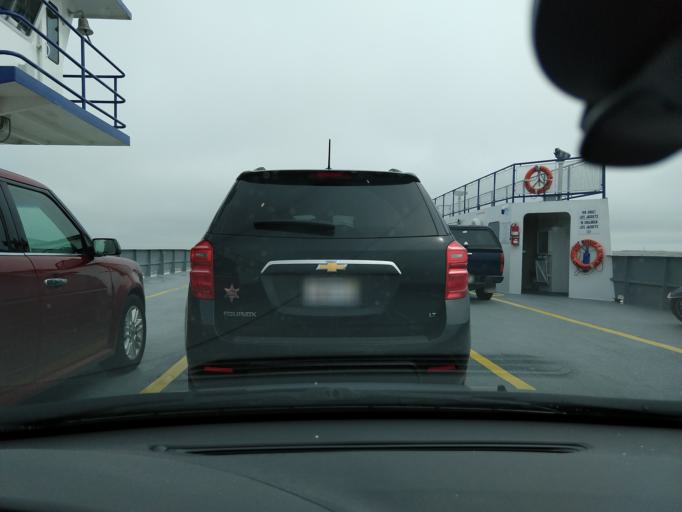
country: US
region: Alabama
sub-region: Mobile County
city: Dauphin Island
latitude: 30.2508
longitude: -88.0583
